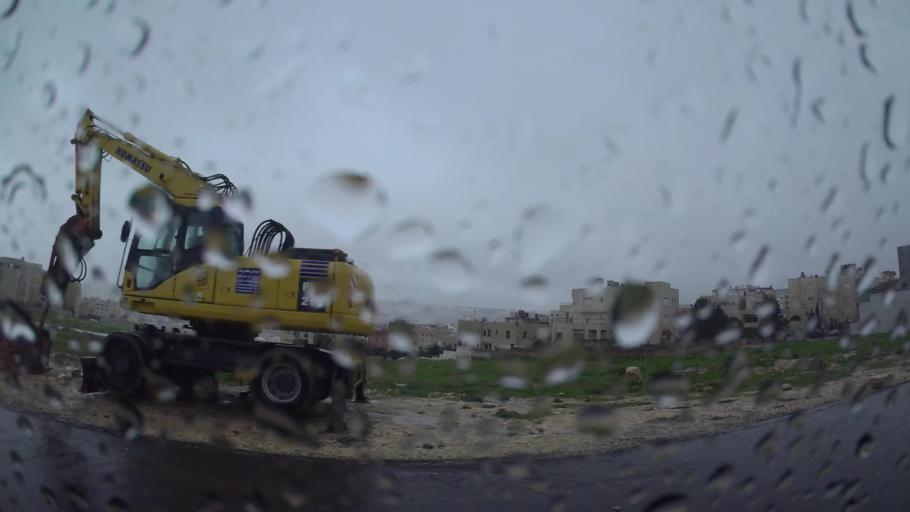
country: JO
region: Amman
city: Al Jubayhah
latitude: 32.0477
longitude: 35.8915
